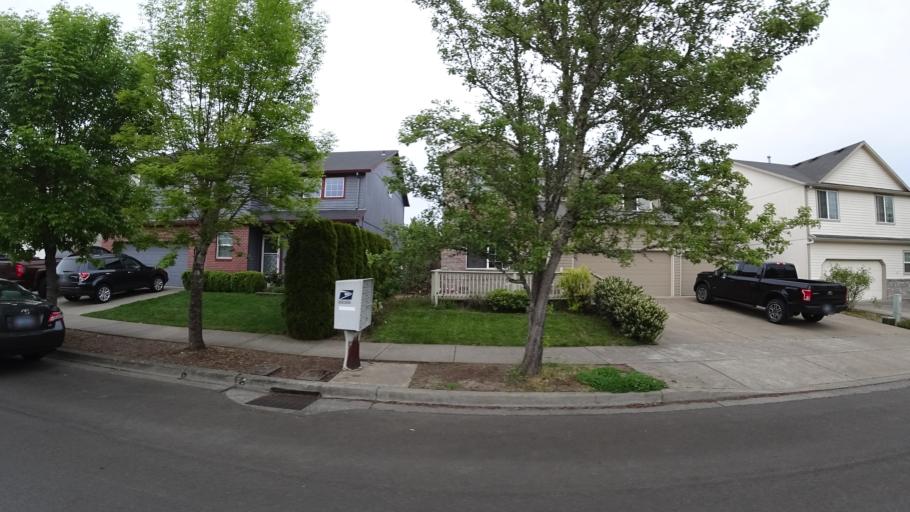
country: US
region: Oregon
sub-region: Washington County
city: Aloha
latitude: 45.5112
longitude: -122.9115
